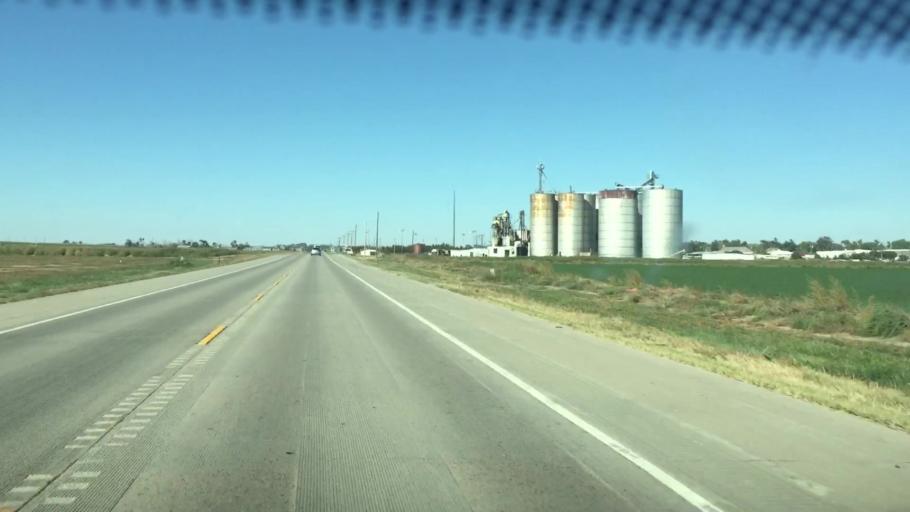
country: US
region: Colorado
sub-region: Prowers County
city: Lamar
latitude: 38.1486
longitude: -102.7234
